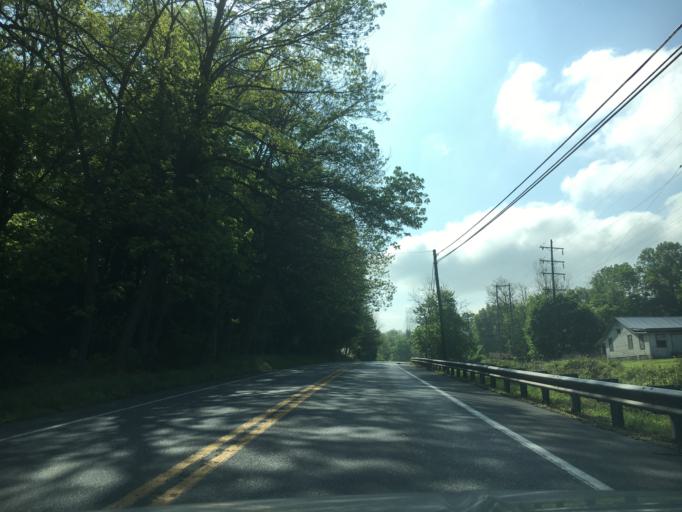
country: US
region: Pennsylvania
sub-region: Berks County
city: Oley
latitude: 40.3731
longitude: -75.7165
